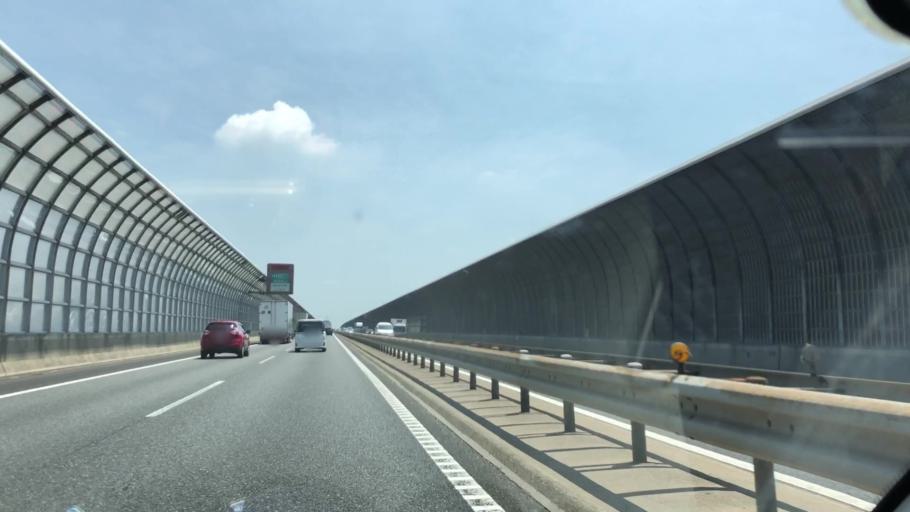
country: JP
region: Saitama
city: Shimotoda
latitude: 35.8467
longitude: 139.7023
